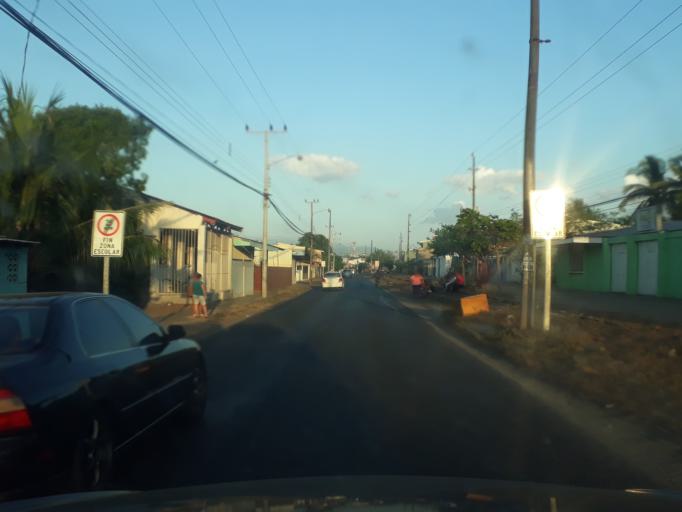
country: CR
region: Puntarenas
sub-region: Canton Central de Puntarenas
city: Puntarenas
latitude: 9.9809
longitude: -84.8091
